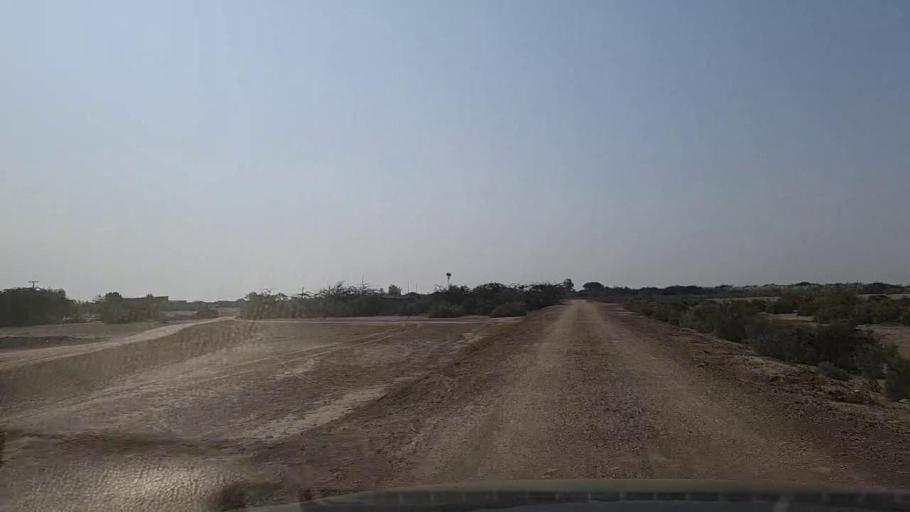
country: PK
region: Sindh
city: Mirpur Sakro
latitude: 24.4248
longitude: 67.7078
